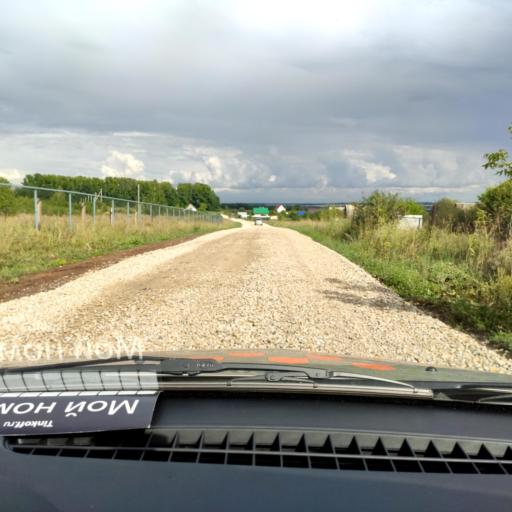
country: RU
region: Bashkortostan
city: Avdon
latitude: 54.5159
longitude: 55.8361
